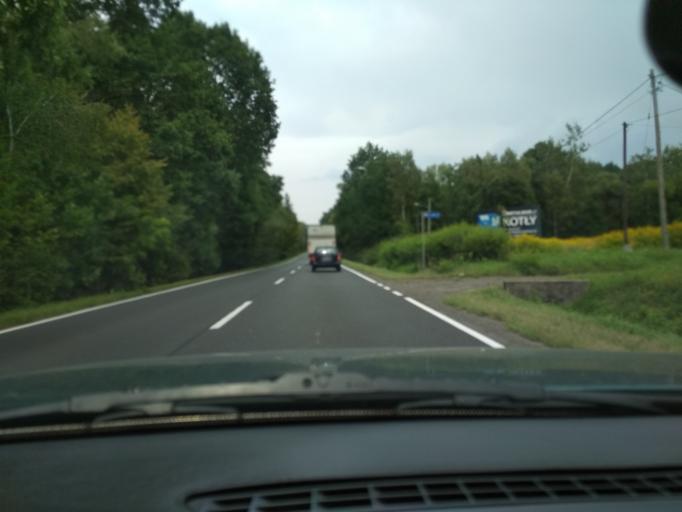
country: PL
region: Silesian Voivodeship
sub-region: Powiat zawiercianski
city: Zawiercie
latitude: 50.4641
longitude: 19.3945
